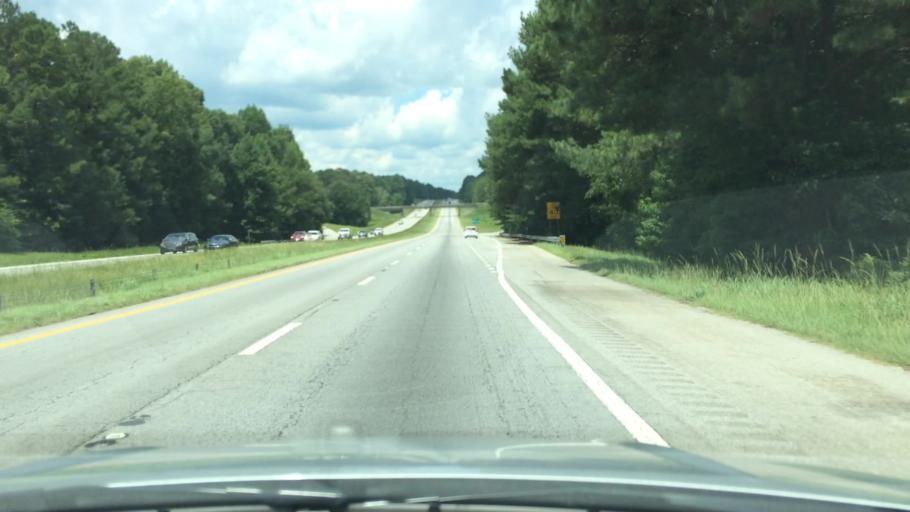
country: US
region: South Carolina
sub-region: Newberry County
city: Newberry
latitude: 34.3759
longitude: -81.6767
